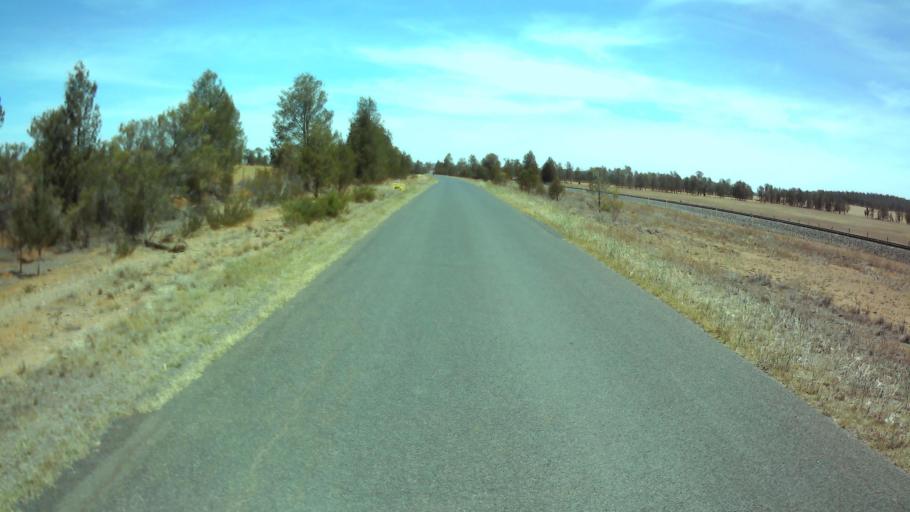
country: AU
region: New South Wales
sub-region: Weddin
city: Grenfell
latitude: -33.7761
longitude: 147.7548
